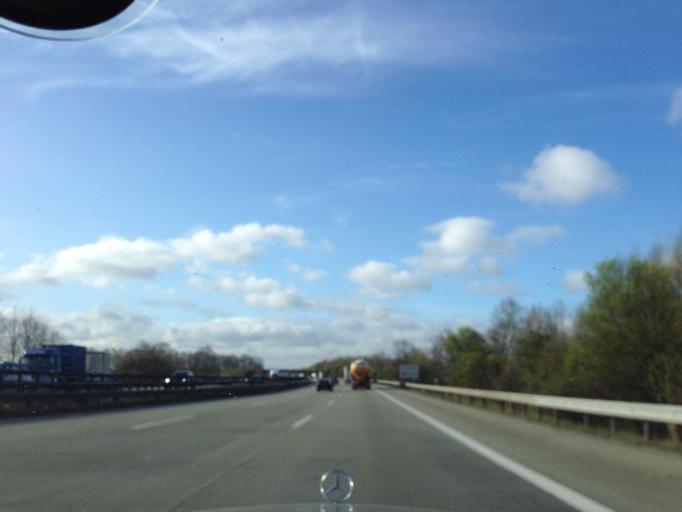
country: DE
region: Hamburg
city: Harburg
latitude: 53.4440
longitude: 10.0297
